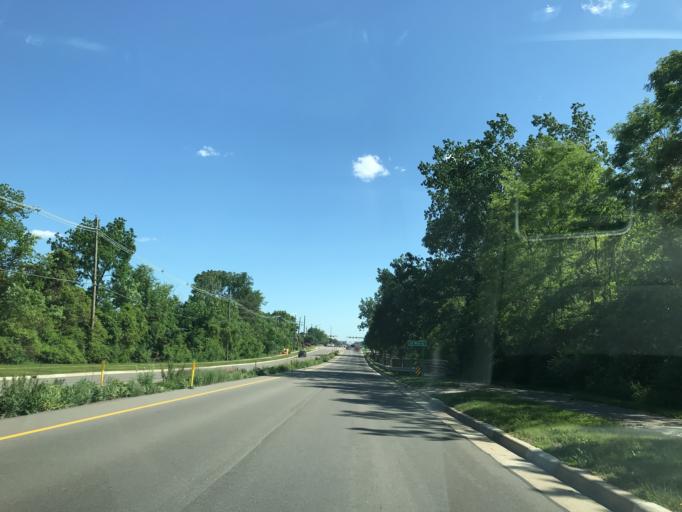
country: US
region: Michigan
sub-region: Oakland County
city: Novi
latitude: 42.4986
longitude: -83.4765
